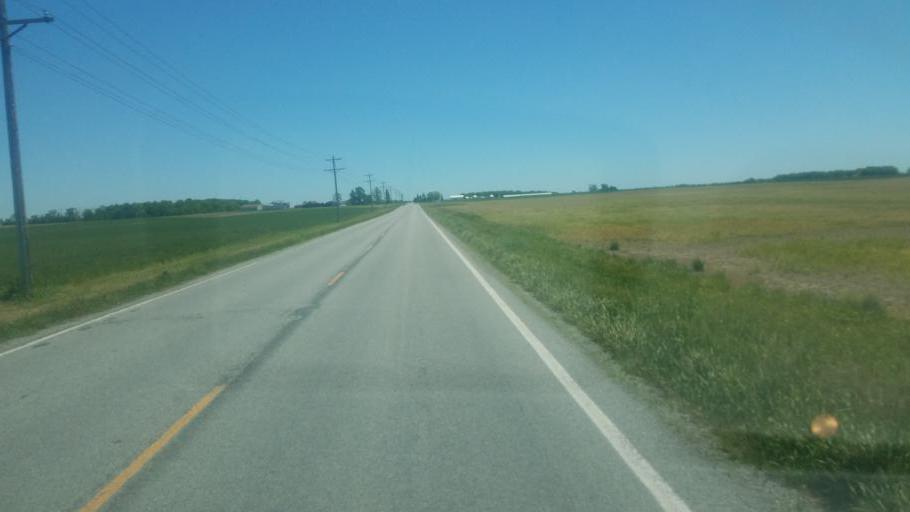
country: US
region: Ohio
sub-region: Miami County
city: Piqua
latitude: 40.2257
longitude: -84.3175
